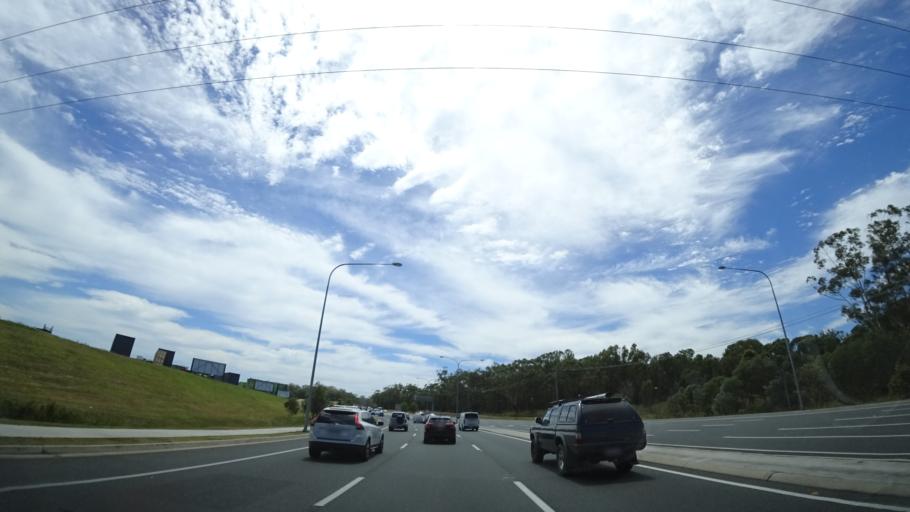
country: AU
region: Queensland
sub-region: Gold Coast
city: Southport
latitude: -27.9649
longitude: 153.3860
